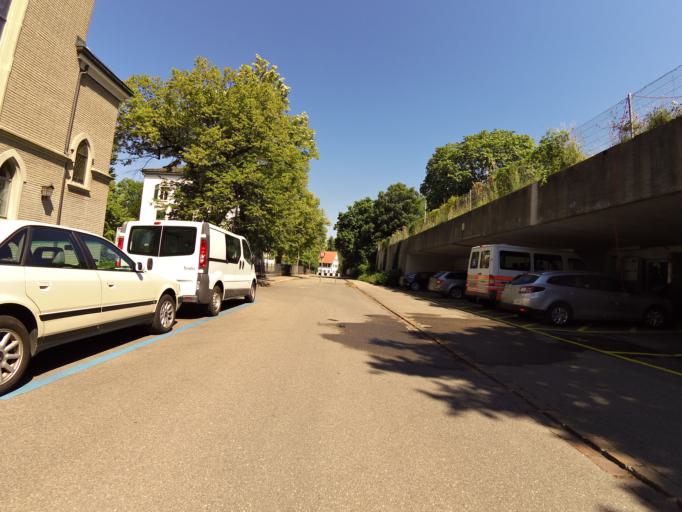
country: CH
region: Zurich
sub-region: Bezirk Zuerich
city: Zuerich (Kreis 6)
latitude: 47.3874
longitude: 8.5423
